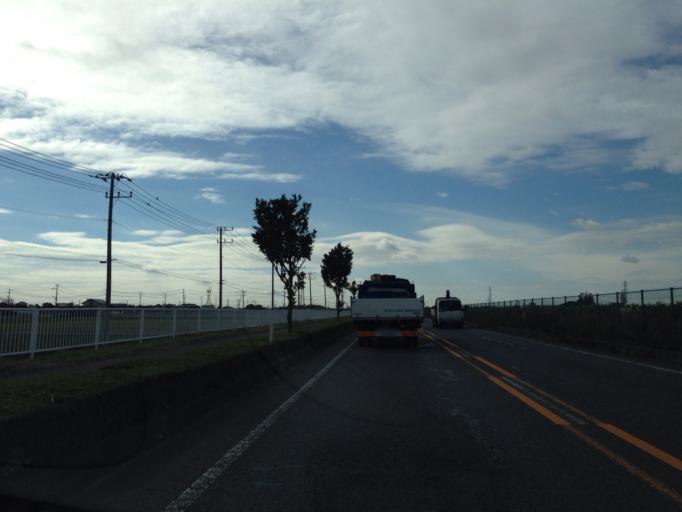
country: JP
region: Ibaraki
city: Fujishiro
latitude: 35.9315
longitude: 140.1203
